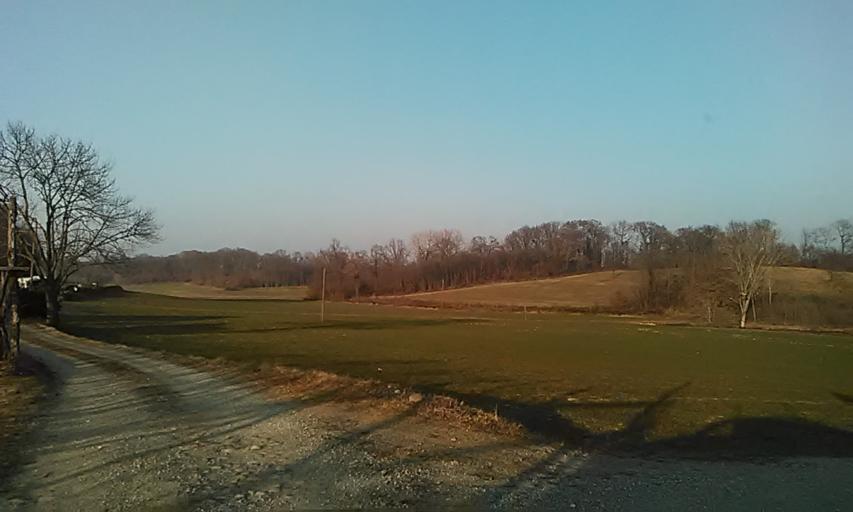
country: IT
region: Piedmont
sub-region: Provincia di Biella
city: Dorzano
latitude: 45.4153
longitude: 8.1216
